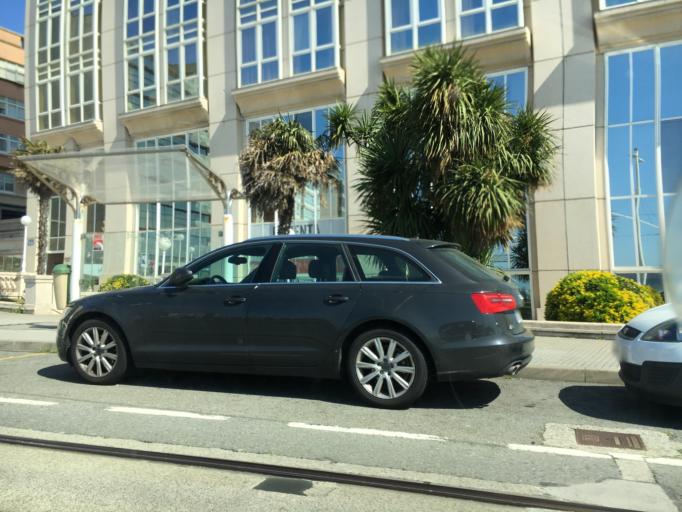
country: ES
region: Galicia
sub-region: Provincia da Coruna
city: A Coruna
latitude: 43.3755
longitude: -8.4030
